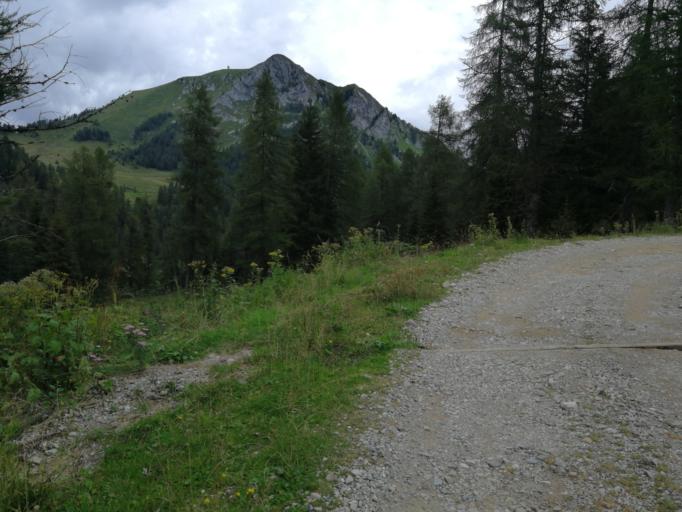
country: IT
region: Trentino-Alto Adige
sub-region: Provincia di Trento
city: Brione
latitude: 45.9372
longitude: 10.5347
